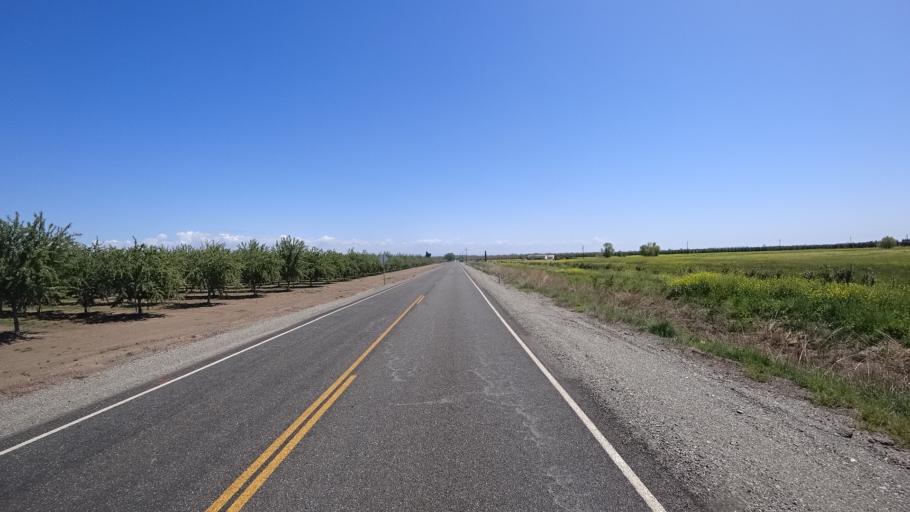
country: US
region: California
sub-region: Glenn County
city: Hamilton City
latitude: 39.7665
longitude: -122.0460
